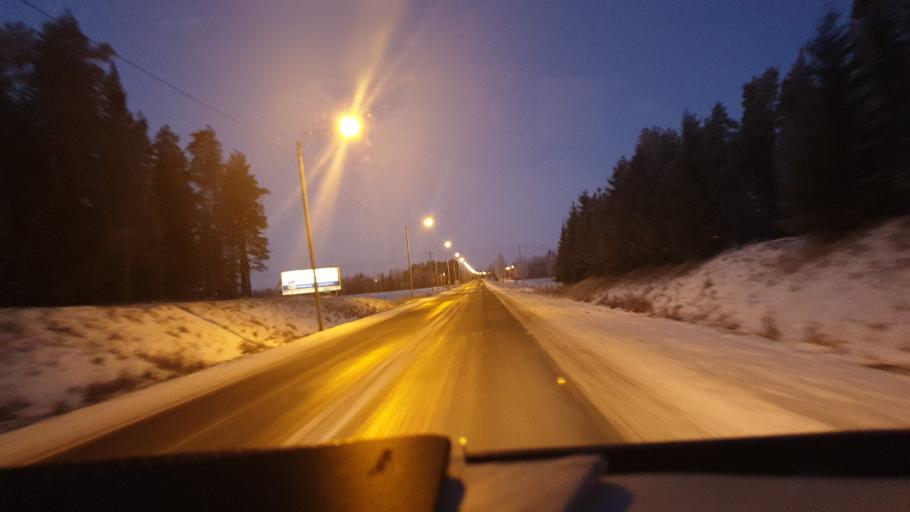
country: FI
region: Northern Ostrobothnia
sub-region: Raahe
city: Raahe
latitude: 64.6893
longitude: 24.6171
